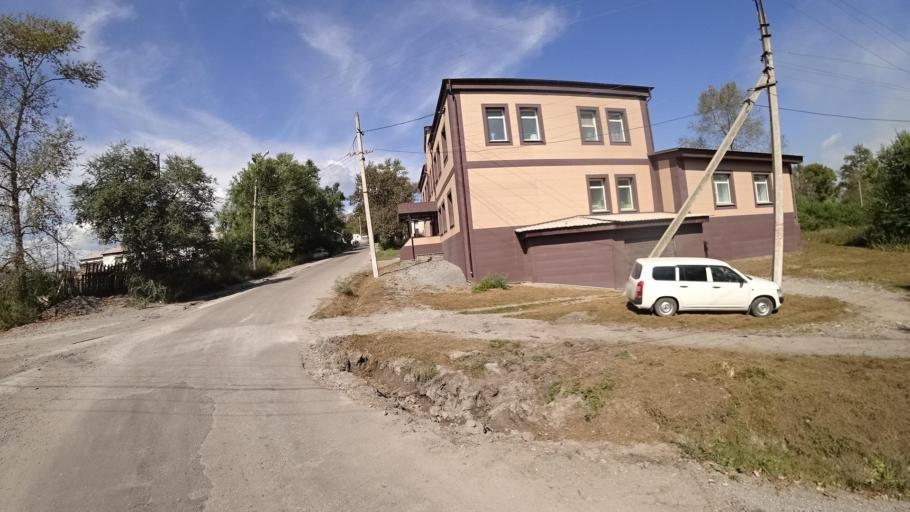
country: RU
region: Jewish Autonomous Oblast
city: Londoko
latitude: 49.0034
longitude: 131.8842
